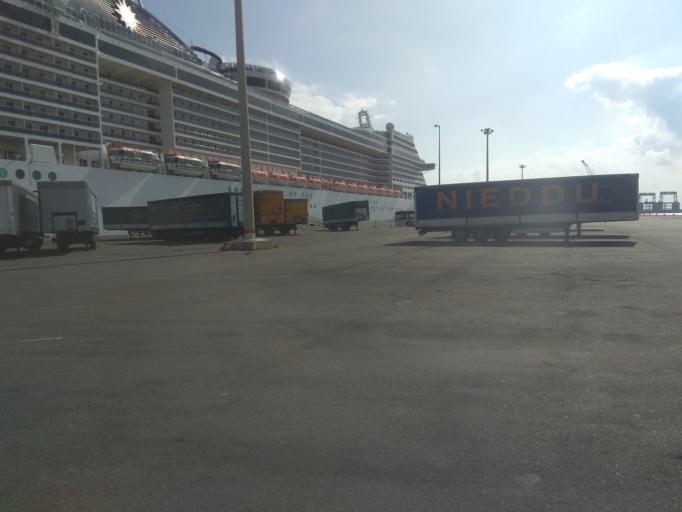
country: IT
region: Sardinia
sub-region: Provincia di Cagliari
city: Cagliari
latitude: 39.2104
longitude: 9.1038
